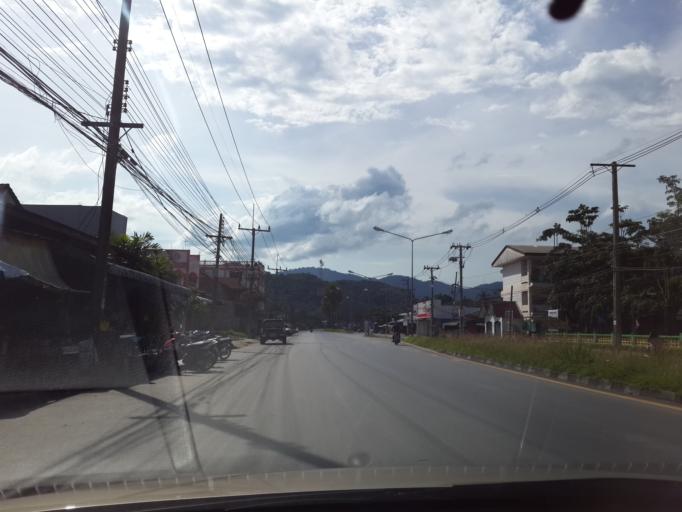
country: TH
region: Yala
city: Krong Pi Nang
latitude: 6.4577
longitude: 101.3416
